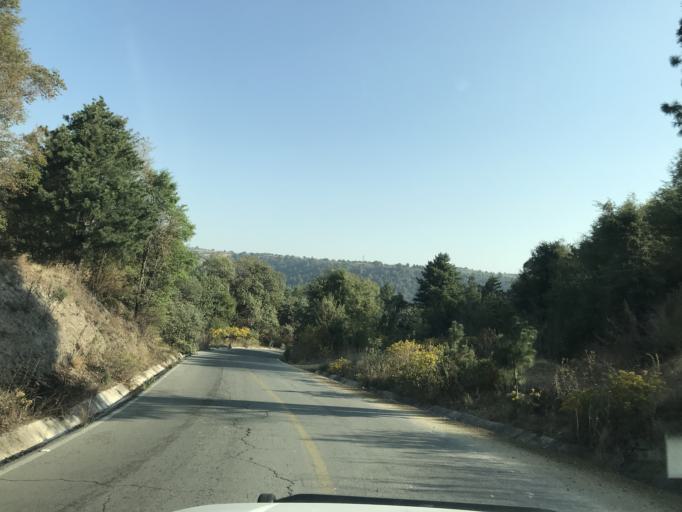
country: MX
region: Puebla
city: San Nicolas de los Ranchos
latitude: 19.0834
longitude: -98.5321
